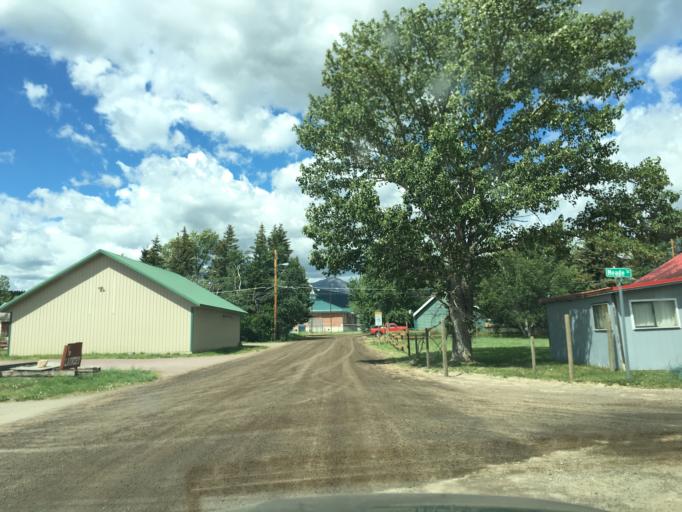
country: US
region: Montana
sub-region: Glacier County
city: South Browning
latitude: 48.4402
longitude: -113.2158
